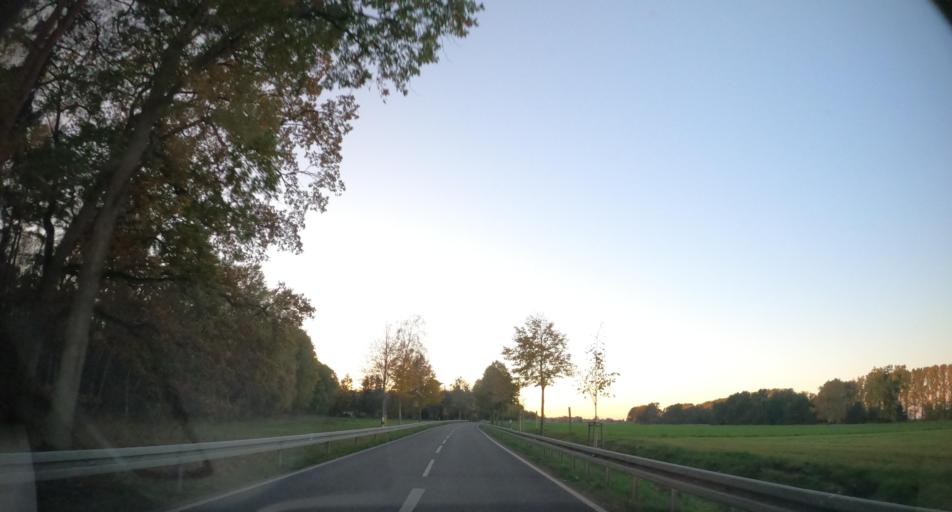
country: DE
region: Mecklenburg-Vorpommern
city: Ueckermunde
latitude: 53.7643
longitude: 13.9912
